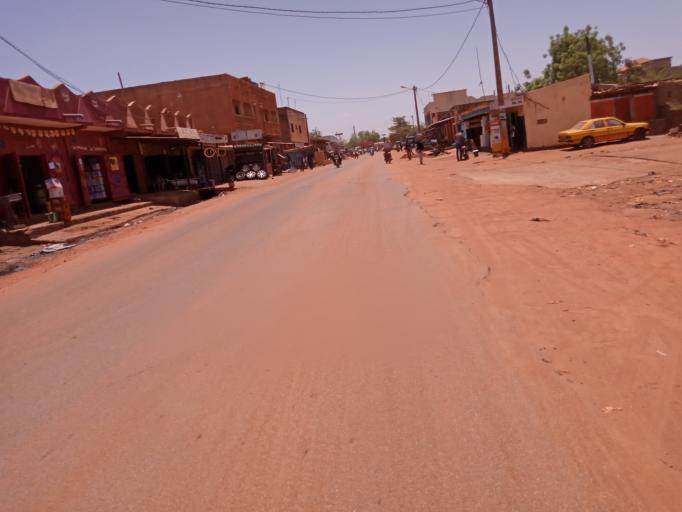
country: ML
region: Bamako
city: Bamako
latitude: 12.5749
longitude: -7.9702
